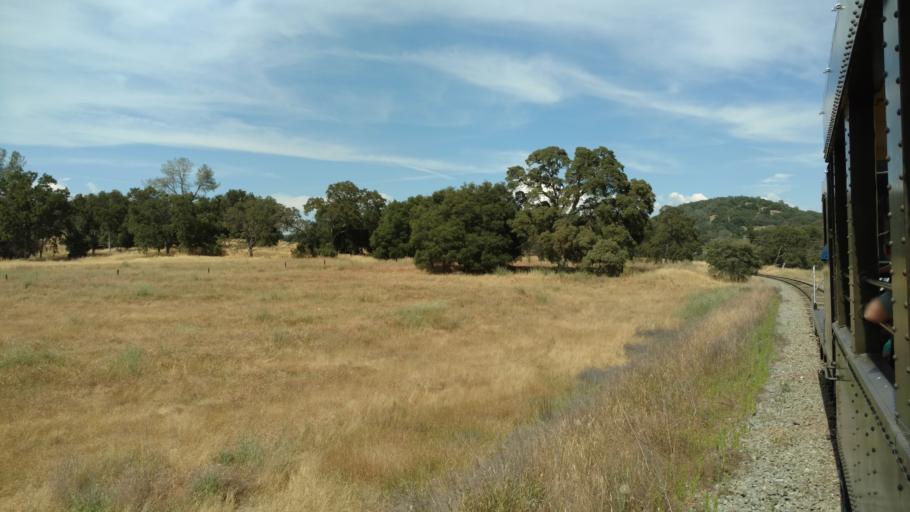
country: US
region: California
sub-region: Tuolumne County
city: Jamestown
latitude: 37.9399
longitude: -120.4224
